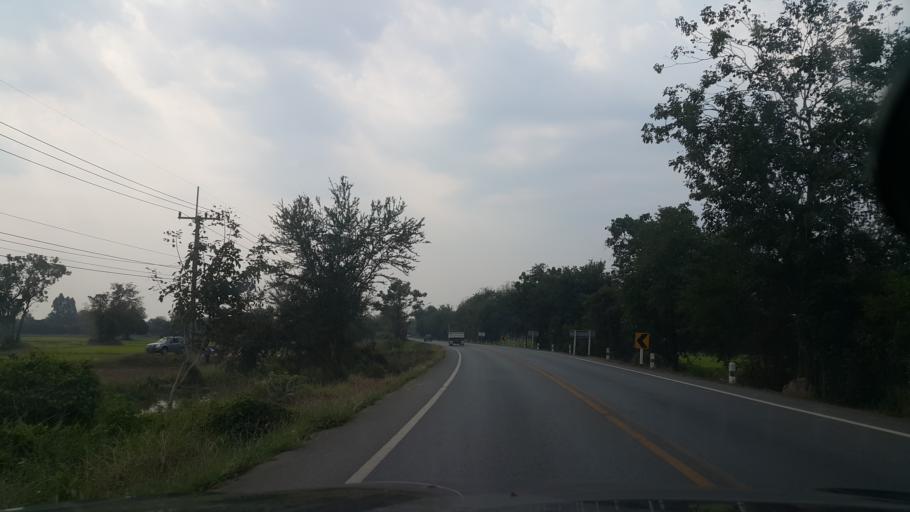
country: TH
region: Sukhothai
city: Si Samrong
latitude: 17.1133
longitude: 99.8896
